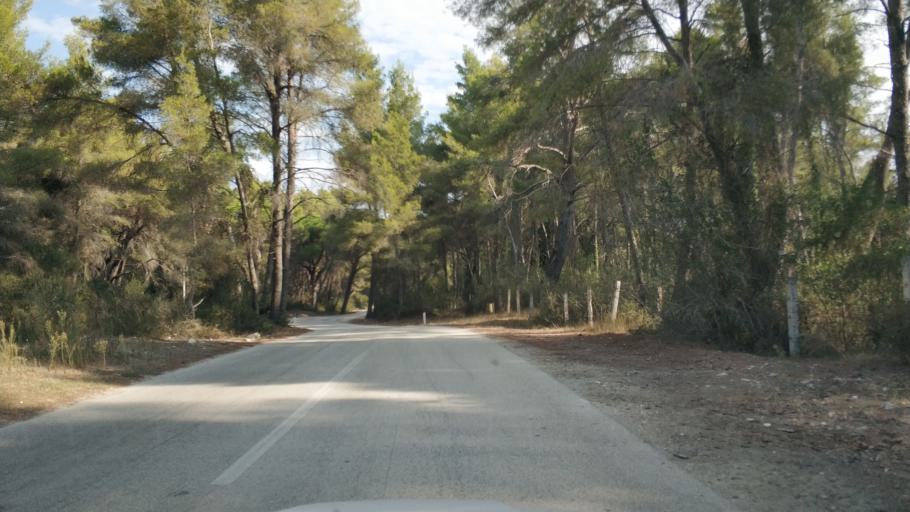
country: AL
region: Fier
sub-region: Rrethi i Lushnjes
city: Divjake
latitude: 40.9795
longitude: 19.4819
